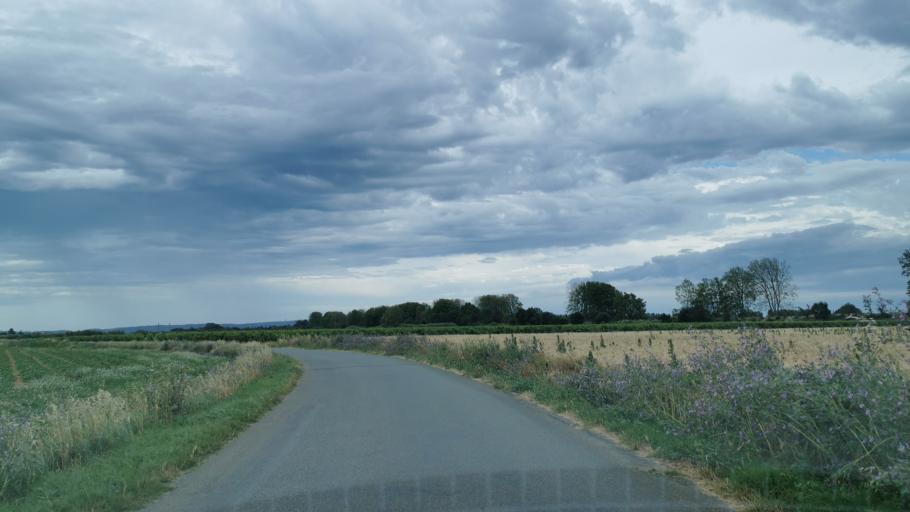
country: FR
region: Languedoc-Roussillon
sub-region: Departement de l'Aude
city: Moussan
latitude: 43.2366
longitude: 2.9890
